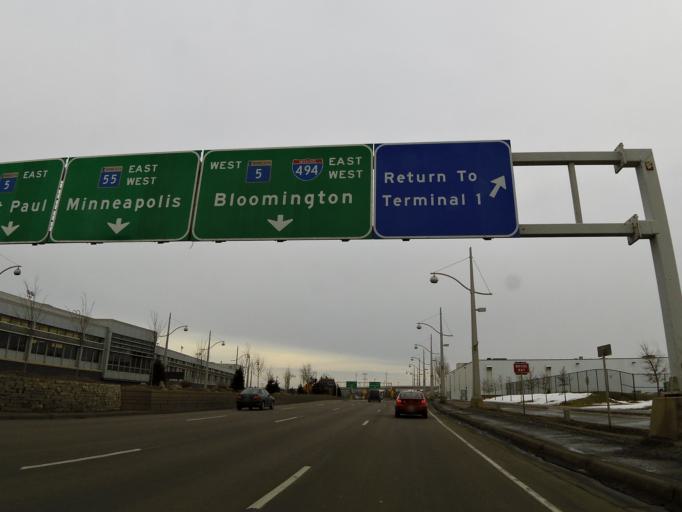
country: US
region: Minnesota
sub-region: Dakota County
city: Mendota Heights
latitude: 44.8792
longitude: -93.1991
